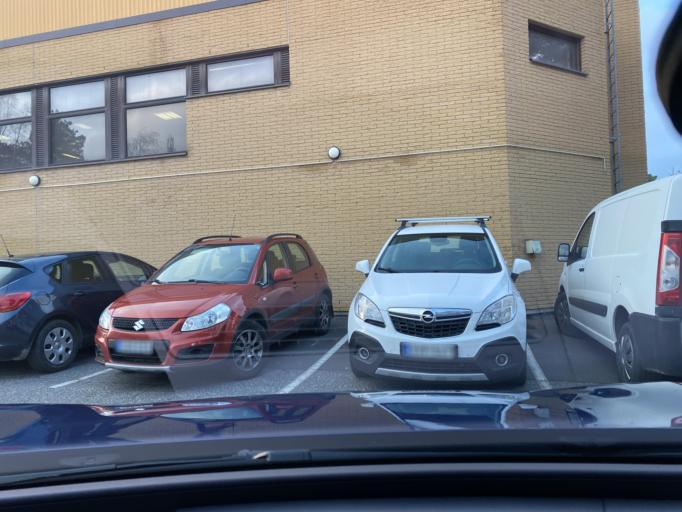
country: FI
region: Varsinais-Suomi
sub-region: Turku
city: Naantali
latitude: 60.4728
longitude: 22.0326
